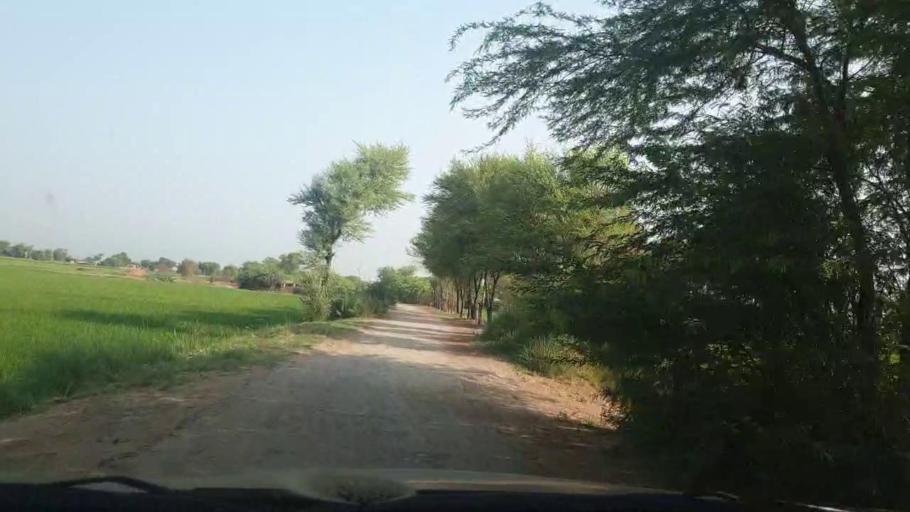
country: PK
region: Sindh
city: Larkana
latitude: 27.5953
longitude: 68.1603
